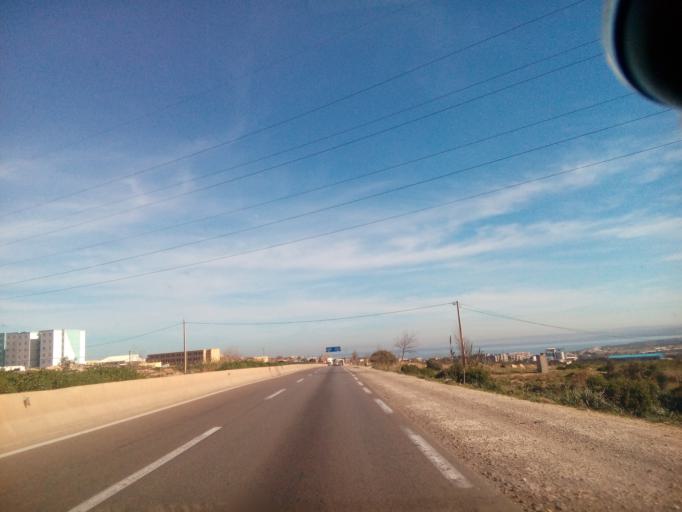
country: DZ
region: Oran
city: Ain el Bya
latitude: 35.7824
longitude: -0.1838
